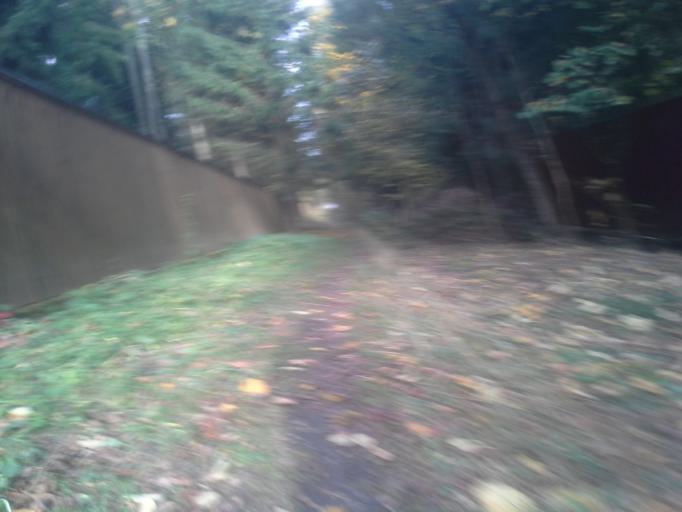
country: RU
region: Moskovskaya
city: Krasnoznamensk
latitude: 55.5774
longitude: 37.0225
